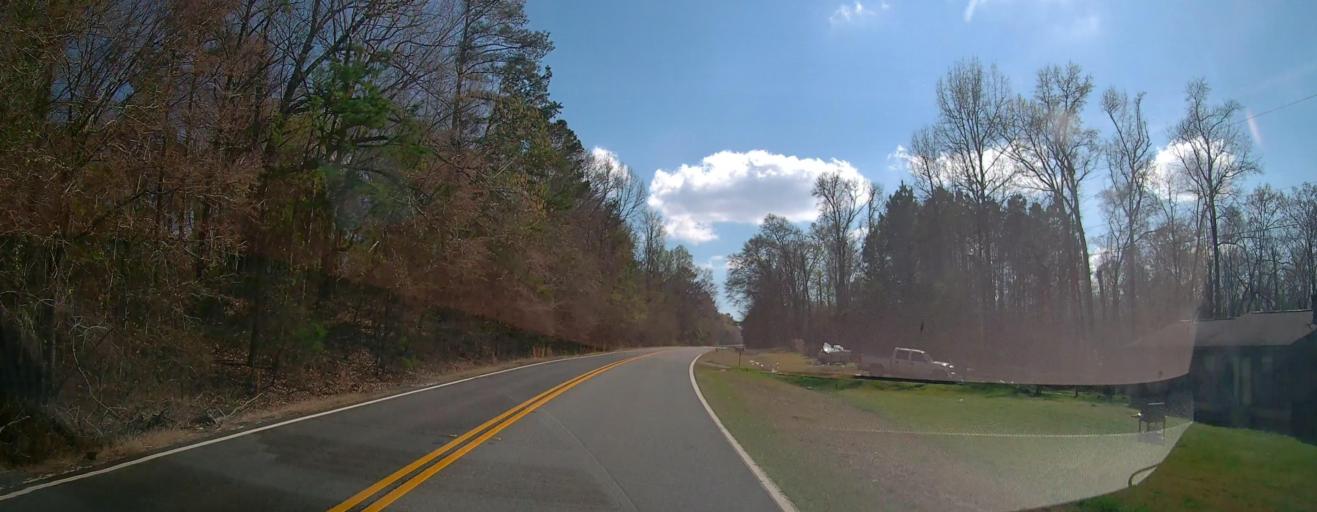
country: US
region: Georgia
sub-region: Twiggs County
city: Jeffersonville
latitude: 32.7215
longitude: -83.3460
